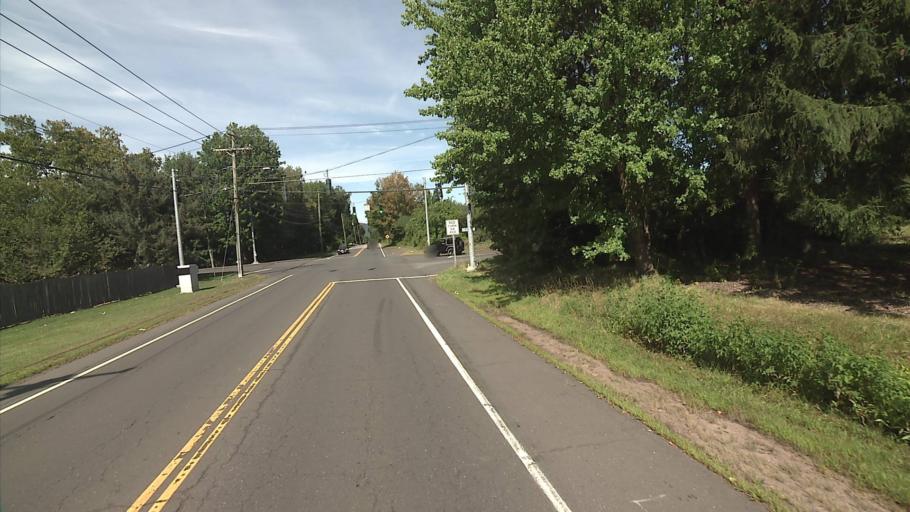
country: US
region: Connecticut
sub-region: New Haven County
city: Cheshire Village
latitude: 41.5118
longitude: -72.8745
